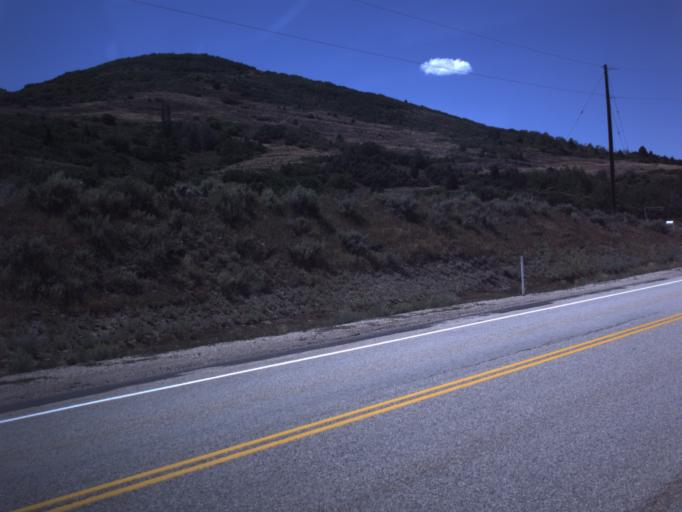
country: US
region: Utah
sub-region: Summit County
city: Francis
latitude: 40.5963
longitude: -111.3537
